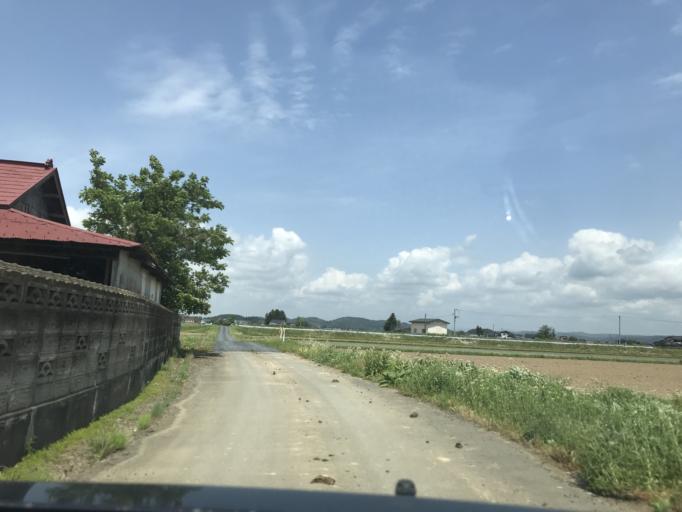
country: JP
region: Miyagi
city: Wakuya
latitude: 38.7077
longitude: 141.2240
